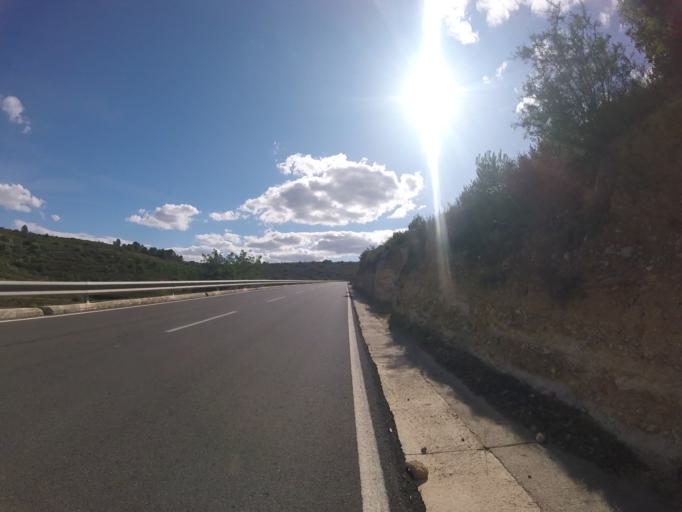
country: ES
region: Valencia
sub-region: Provincia de Castello
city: Cuevas de Vinroma
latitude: 40.3166
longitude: 0.1343
